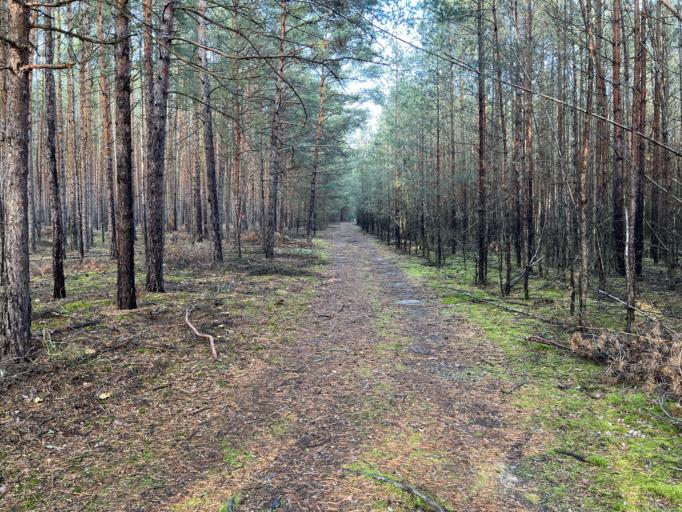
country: DE
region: Brandenburg
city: Schwerin
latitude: 52.1393
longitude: 13.6394
